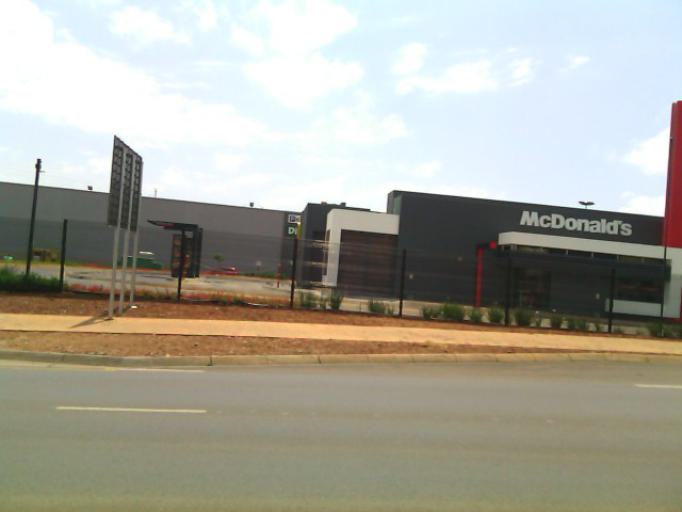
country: ZA
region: Gauteng
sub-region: City of Tshwane Metropolitan Municipality
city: Centurion
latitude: -25.8419
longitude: 28.1862
